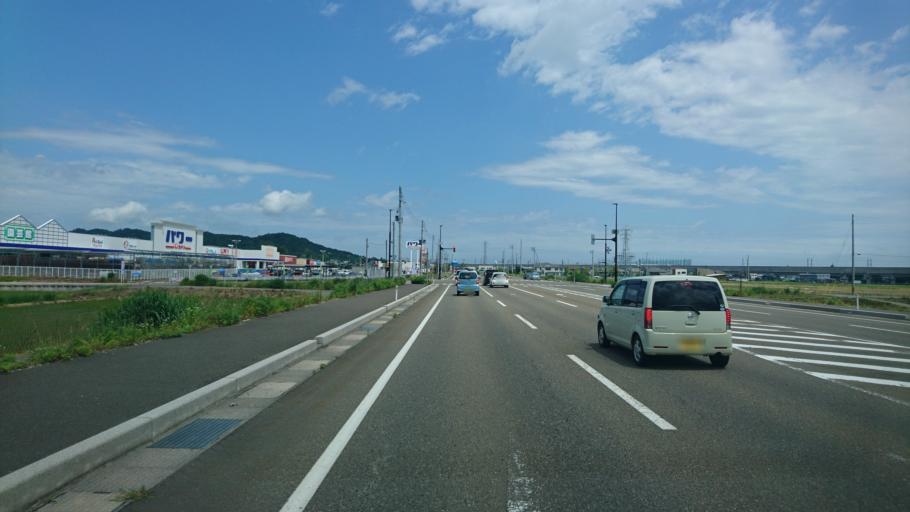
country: JP
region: Niigata
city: Joetsu
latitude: 37.0878
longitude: 138.2335
